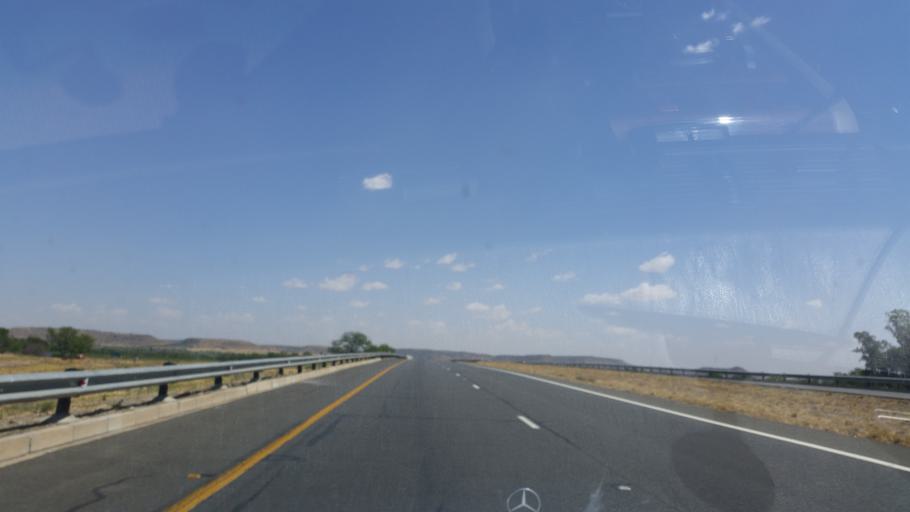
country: ZA
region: Orange Free State
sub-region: Mangaung Metropolitan Municipality
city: Bloemfontein
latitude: -28.9649
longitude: 26.3491
